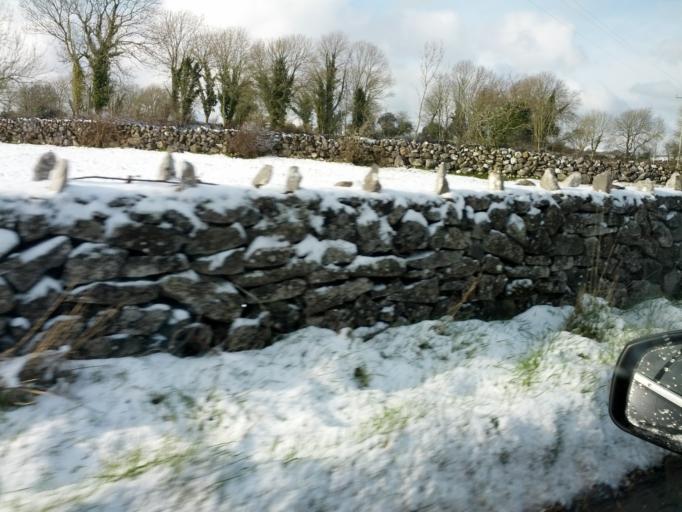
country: IE
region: Connaught
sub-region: County Galway
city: Athenry
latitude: 53.2062
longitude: -8.7591
